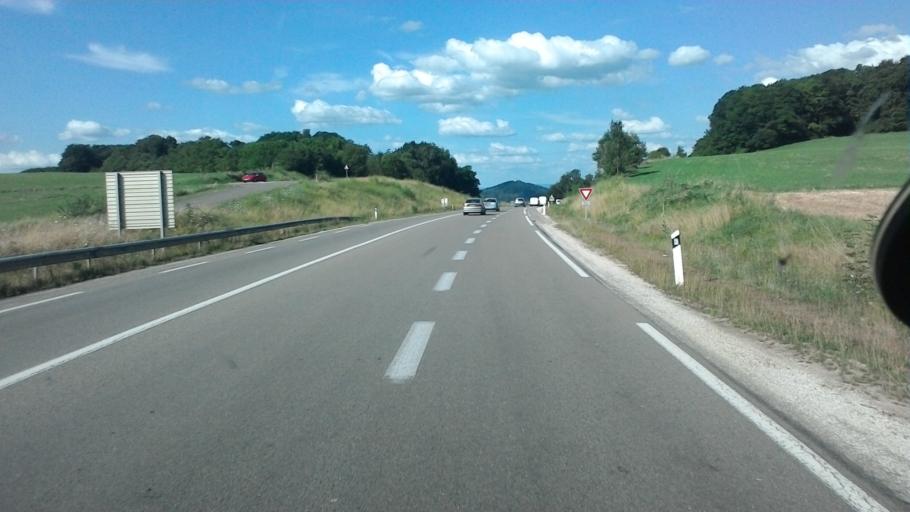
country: FR
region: Franche-Comte
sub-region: Departement de la Haute-Saone
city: Noidans-les-Vesoul
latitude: 47.6001
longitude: 6.1133
